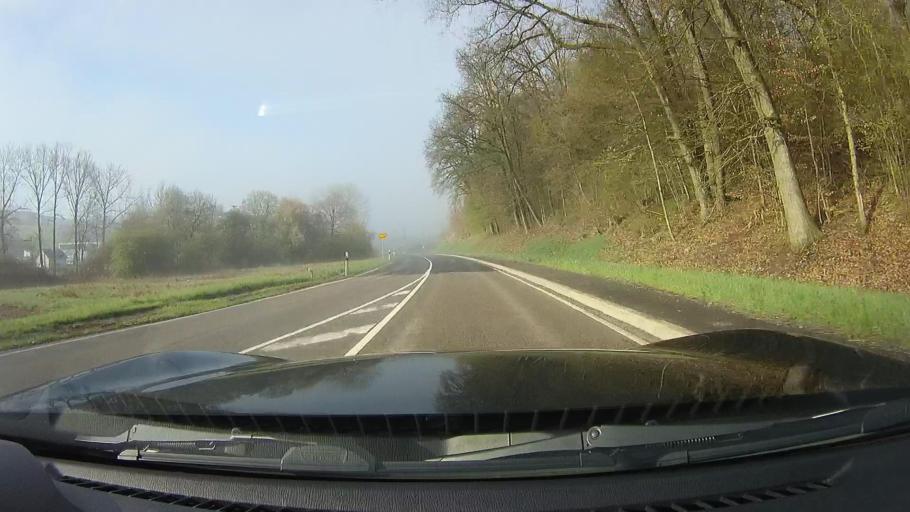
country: DE
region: Baden-Wuerttemberg
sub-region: Karlsruhe Region
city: Osterburken
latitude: 49.4225
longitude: 9.4125
